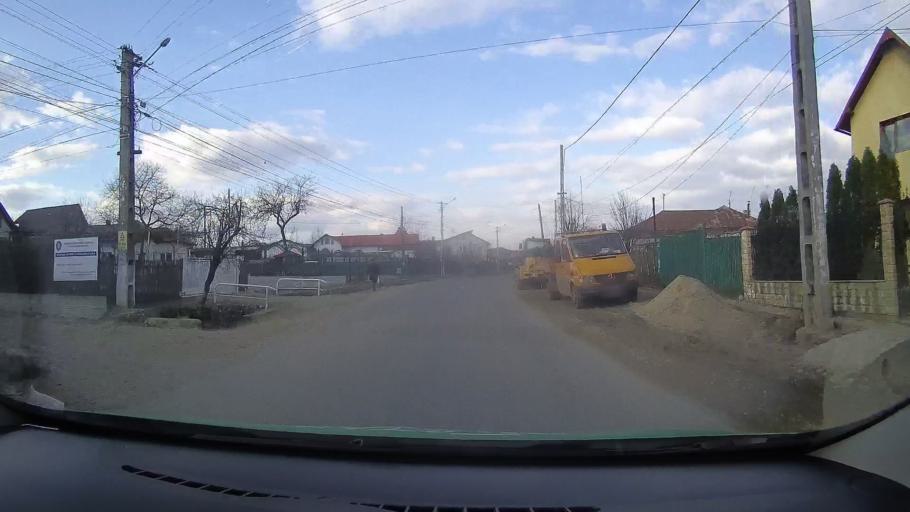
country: RO
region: Dambovita
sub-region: Comuna Gura Ocnitei
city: Gura Ocnitei
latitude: 44.9349
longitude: 25.5620
